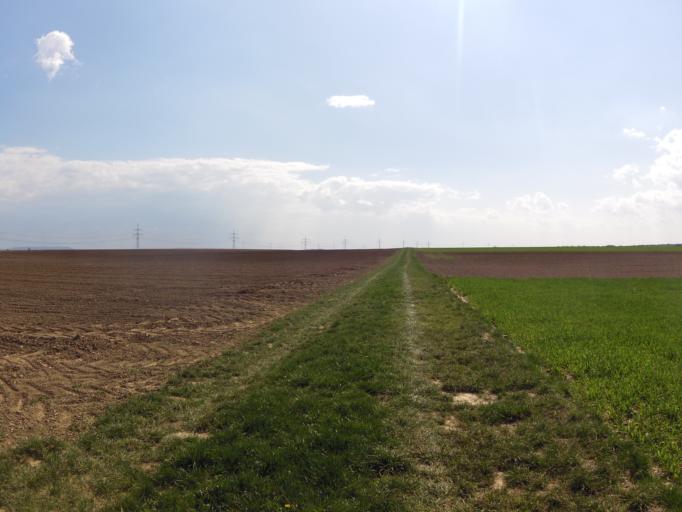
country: DE
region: Bavaria
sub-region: Regierungsbezirk Unterfranken
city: Oberpleichfeld
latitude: 49.8469
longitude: 10.0826
